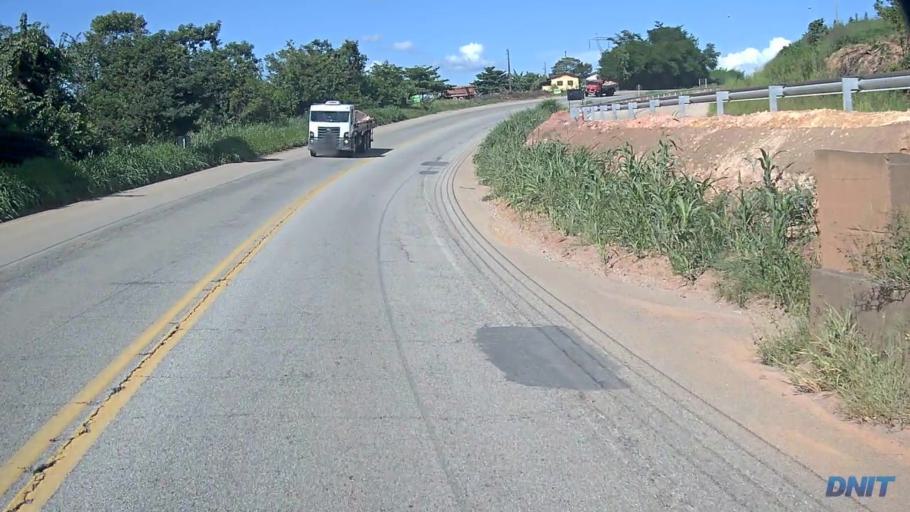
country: BR
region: Minas Gerais
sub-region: Caete
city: Caete
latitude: -19.7361
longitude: -43.5157
